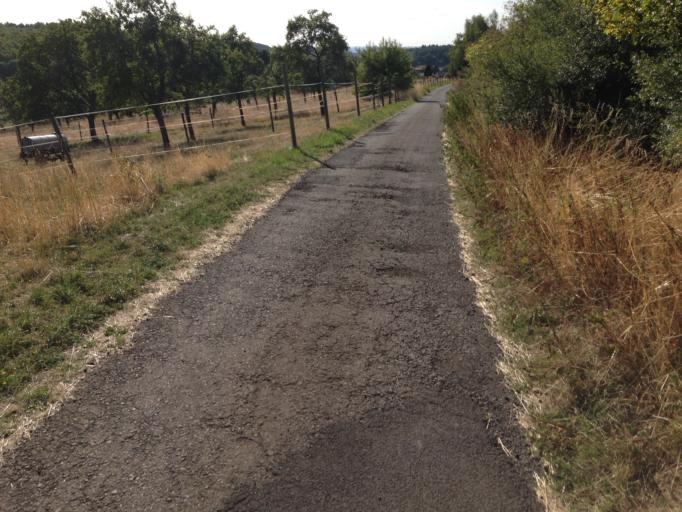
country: DE
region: Hesse
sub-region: Regierungsbezirk Giessen
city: Reiskirchen
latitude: 50.6172
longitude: 8.8597
